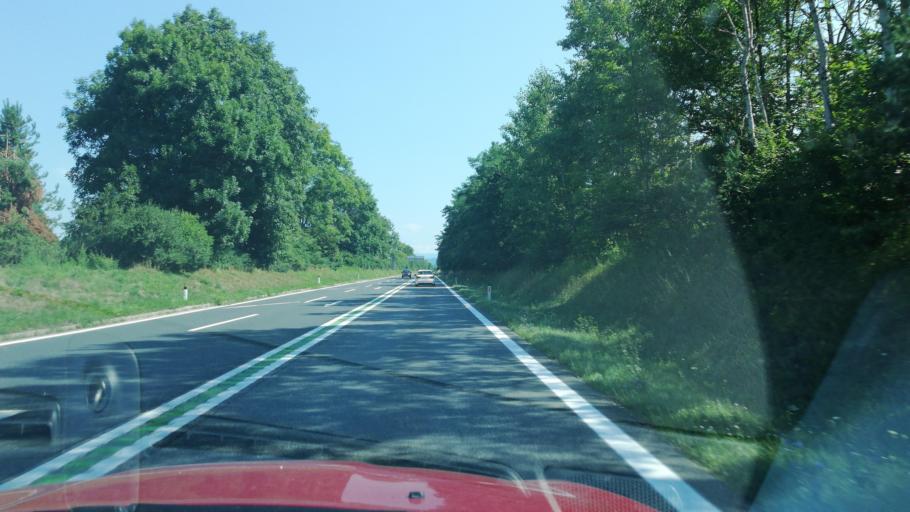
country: AT
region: Carinthia
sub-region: Politischer Bezirk Klagenfurt Land
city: Maria Saal
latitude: 46.6725
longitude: 14.3234
